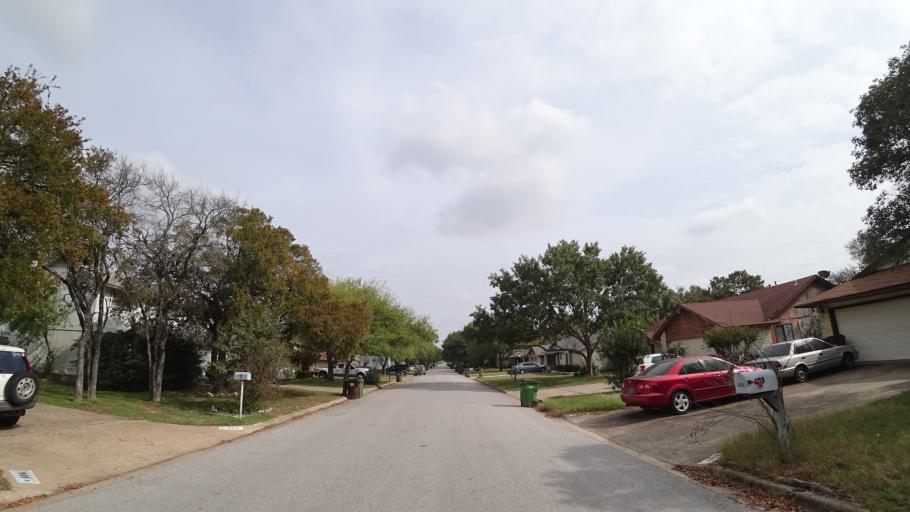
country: US
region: Texas
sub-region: Williamson County
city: Round Rock
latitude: 30.4928
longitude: -97.6850
